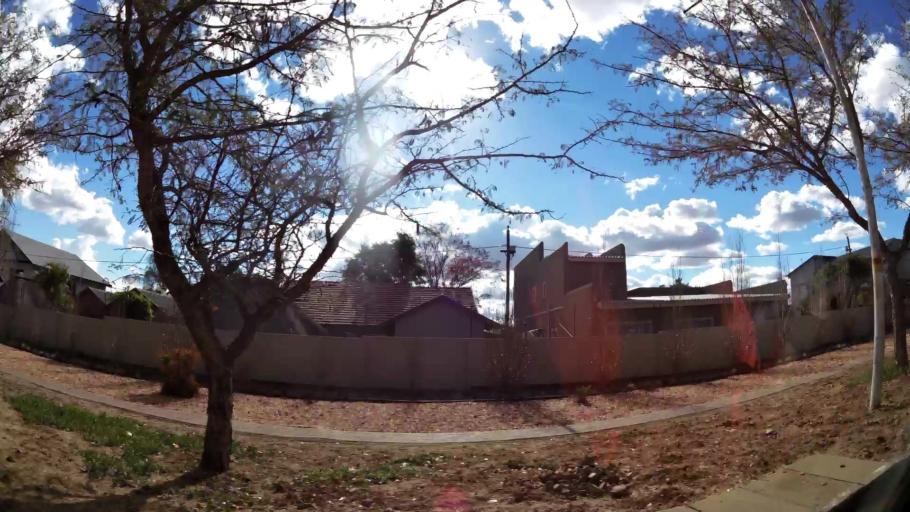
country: ZA
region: Limpopo
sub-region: Capricorn District Municipality
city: Polokwane
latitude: -23.8879
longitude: 29.4803
